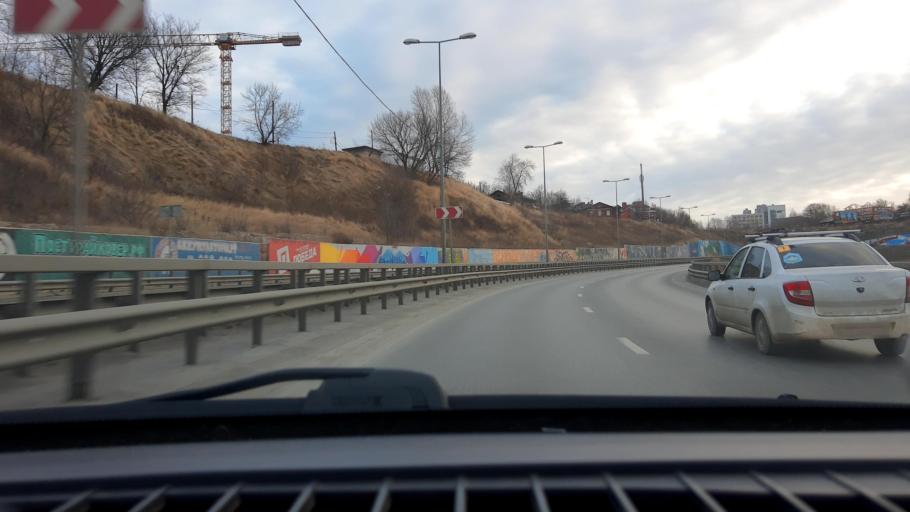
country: RU
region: Nizjnij Novgorod
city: Nizhniy Novgorod
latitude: 56.3147
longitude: 43.9751
